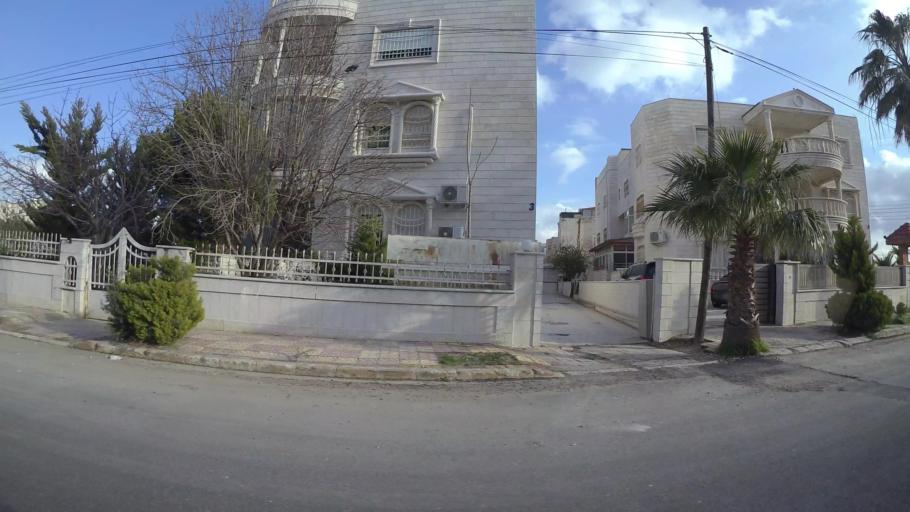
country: JO
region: Amman
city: Al Bunayyat ash Shamaliyah
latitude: 31.9095
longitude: 35.8804
